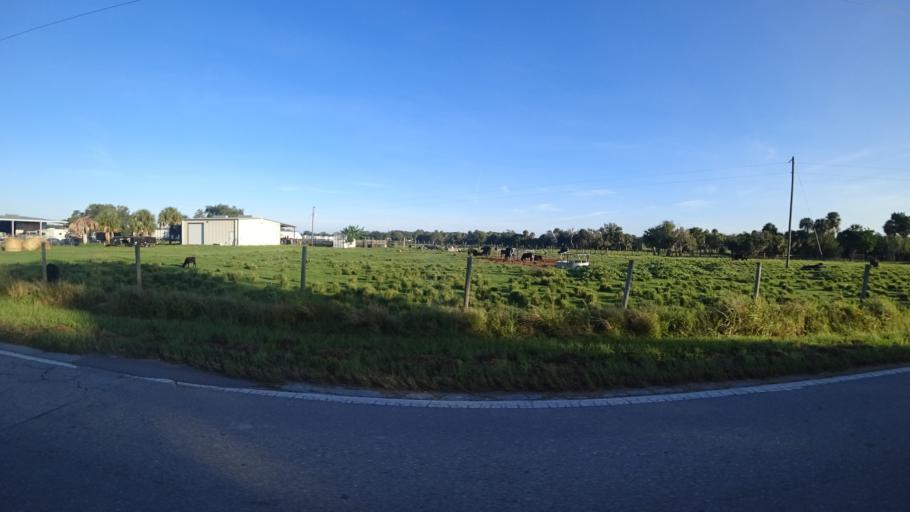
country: US
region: Florida
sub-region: Manatee County
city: Ellenton
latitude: 27.5284
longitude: -82.5383
